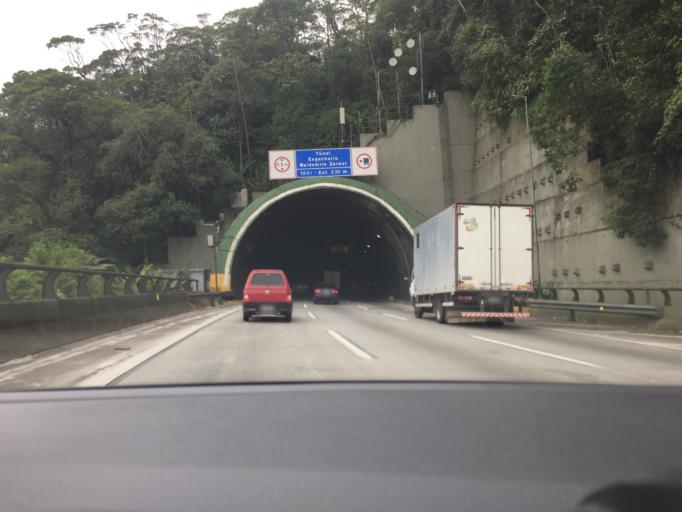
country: BR
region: Sao Paulo
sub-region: Cubatao
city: Cubatao
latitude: -23.9228
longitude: -46.5334
